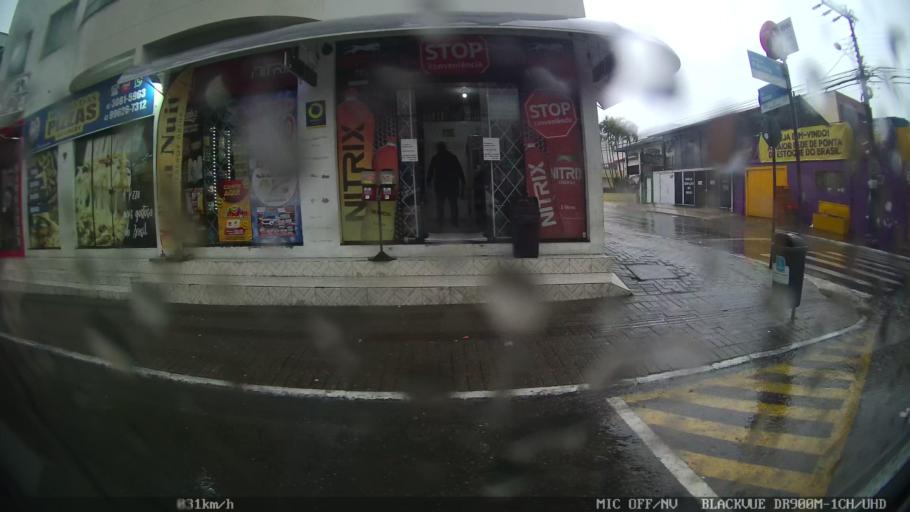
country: BR
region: Santa Catarina
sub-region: Balneario Camboriu
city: Balneario Camboriu
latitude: -26.9790
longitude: -48.6467
